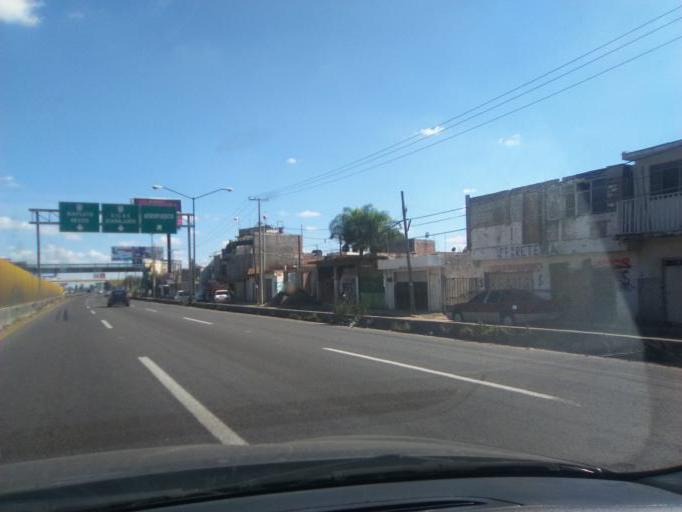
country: MX
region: Guanajuato
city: Colonia Nuevo Mexico
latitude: 20.9837
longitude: -101.4837
